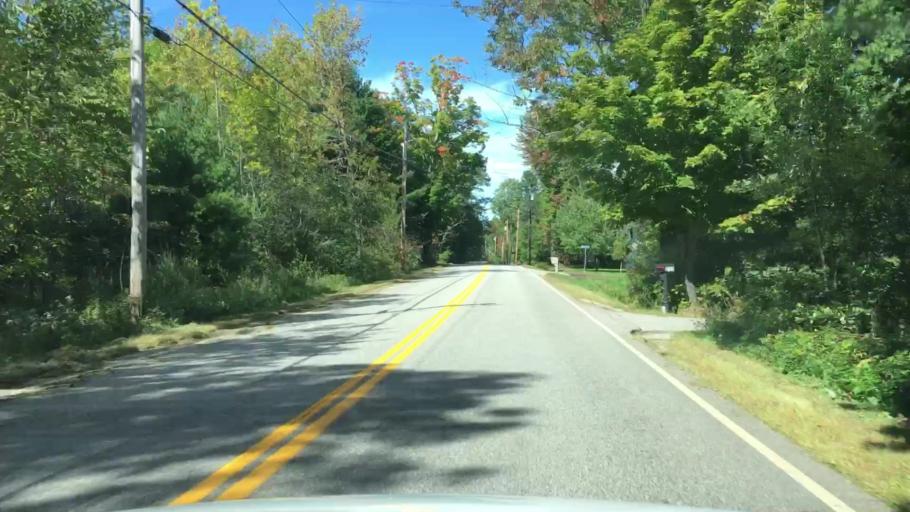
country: US
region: Maine
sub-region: Cumberland County
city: West Scarborough
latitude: 43.6205
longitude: -70.4070
